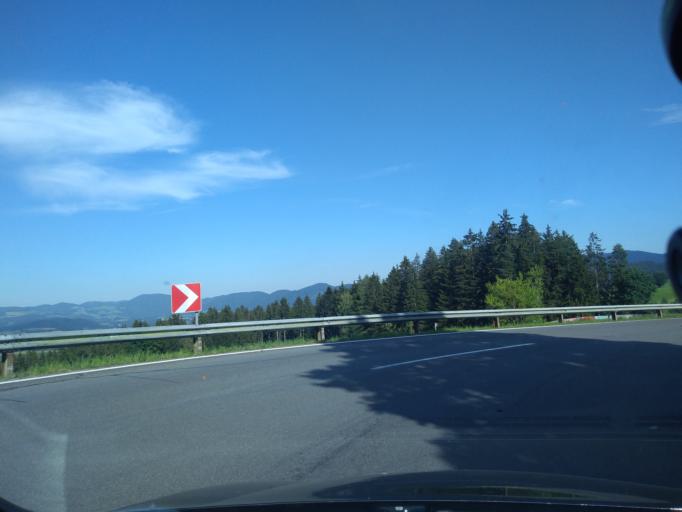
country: AT
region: Styria
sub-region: Politischer Bezirk Graz-Umgebung
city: Semriach
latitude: 47.2696
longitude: 15.4251
